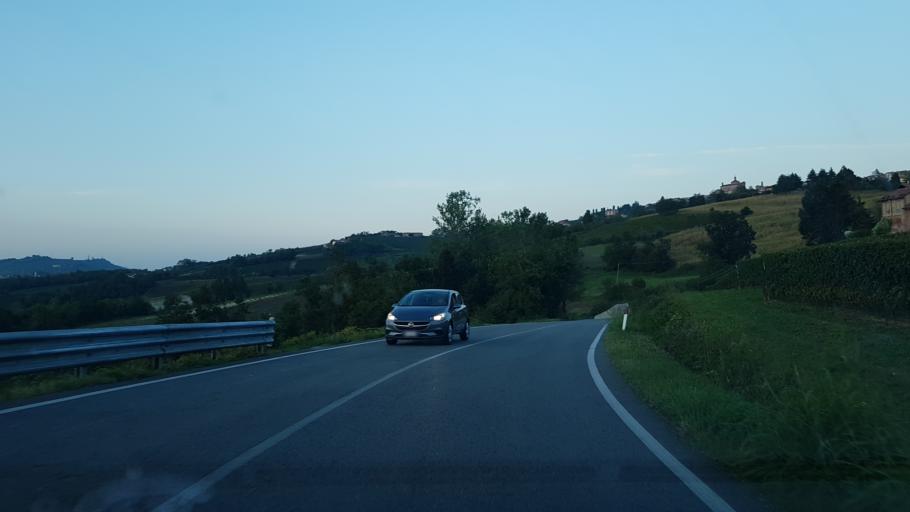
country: IT
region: Piedmont
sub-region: Provincia di Cuneo
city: Novello
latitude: 44.5834
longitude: 7.9140
